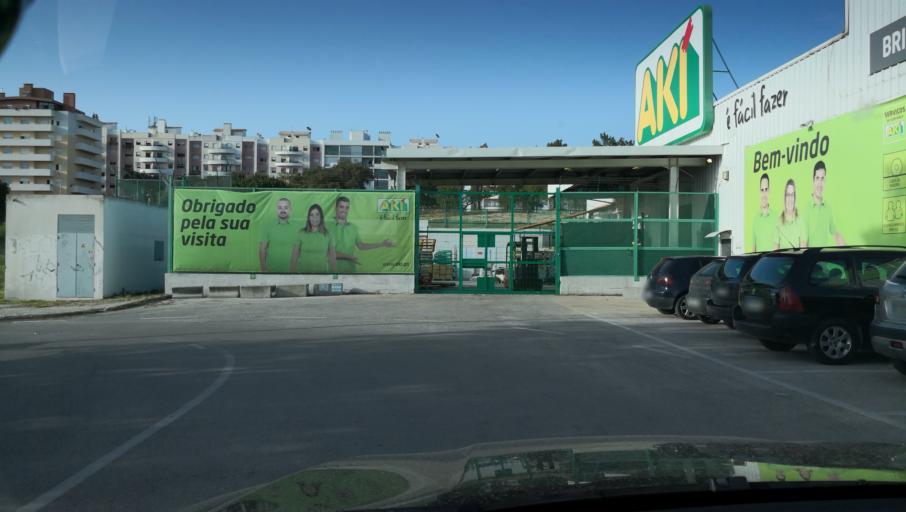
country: PT
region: Setubal
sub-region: Setubal
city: Setubal
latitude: 38.5393
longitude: -8.8753
